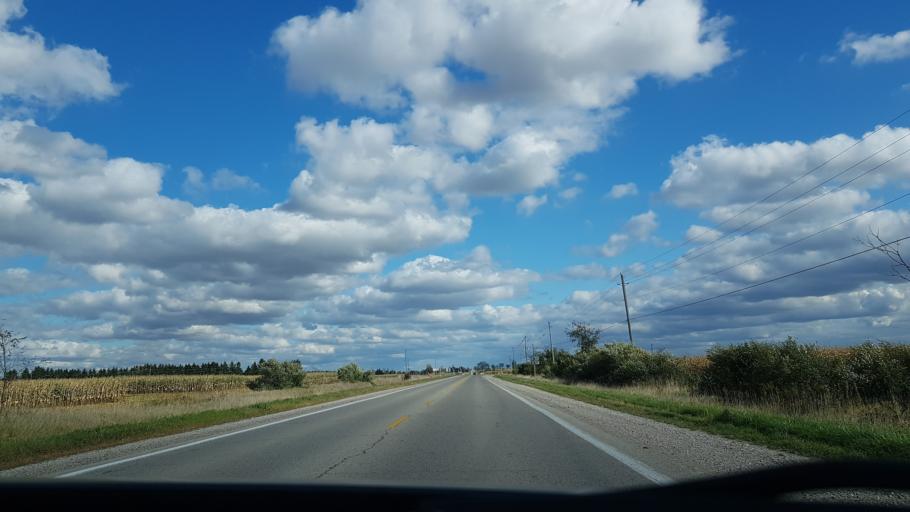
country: CA
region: Ontario
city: South Huron
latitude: 43.1499
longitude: -81.6667
